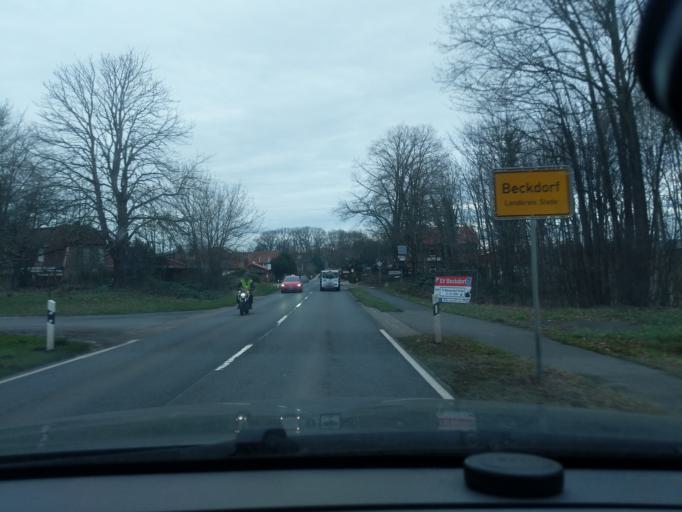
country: DE
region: Lower Saxony
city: Beckdorf
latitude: 53.4078
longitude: 9.6102
